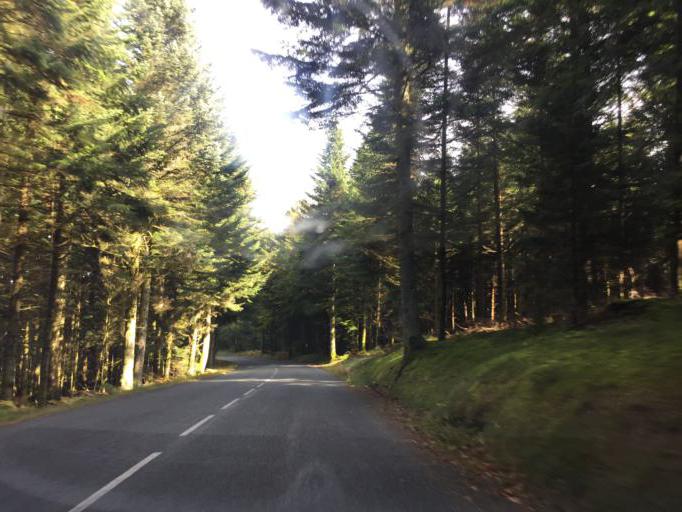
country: FR
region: Rhone-Alpes
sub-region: Departement de la Loire
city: Belmont-de-la-Loire
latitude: 46.1416
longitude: 4.4178
